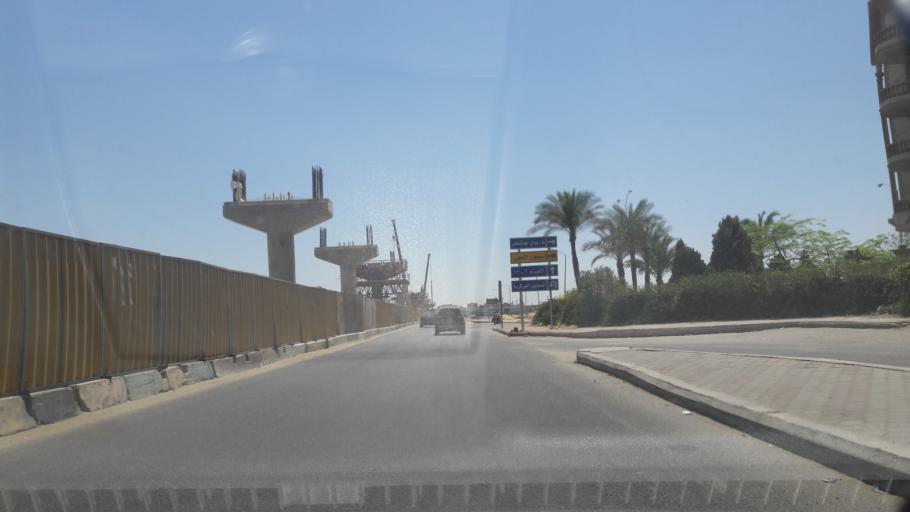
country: EG
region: Al Jizah
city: Madinat Sittah Uktubar
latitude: 29.9704
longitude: 30.9348
